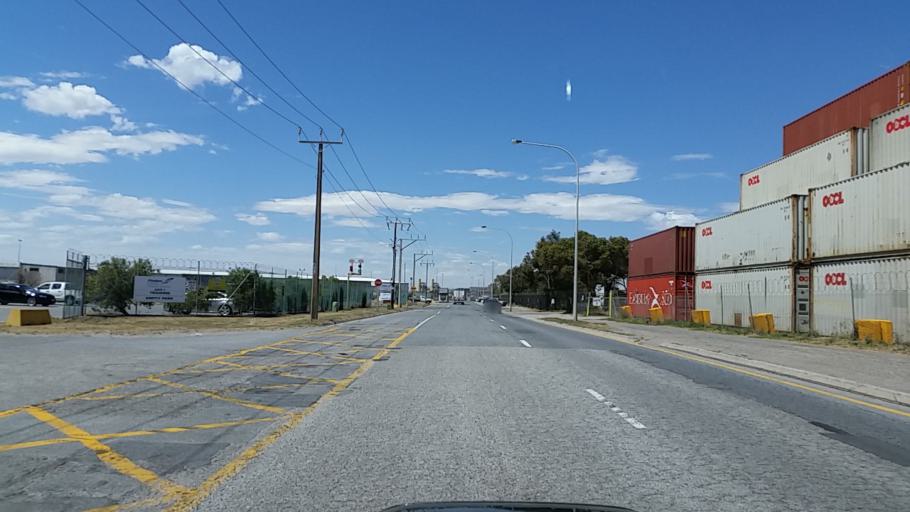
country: AU
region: South Australia
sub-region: Port Adelaide Enfield
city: Birkenhead
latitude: -34.7741
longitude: 138.4928
